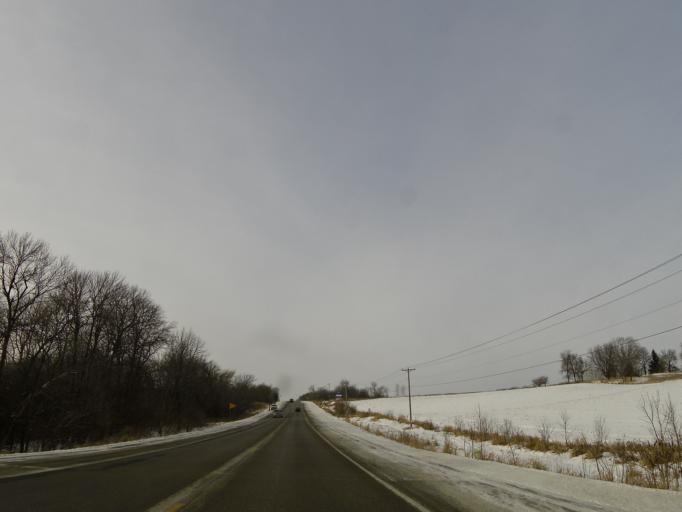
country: US
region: Minnesota
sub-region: Carver County
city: Victoria
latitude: 44.8913
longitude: -93.6906
